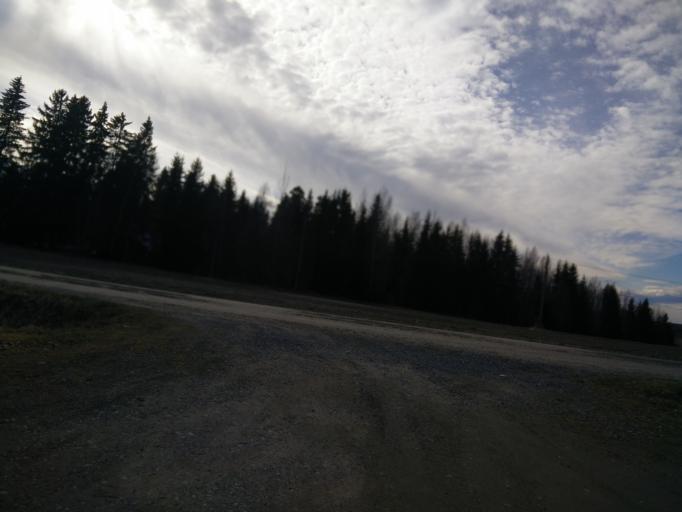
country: FI
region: Pirkanmaa
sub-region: Tampere
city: Orivesi
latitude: 61.6957
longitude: 24.3624
